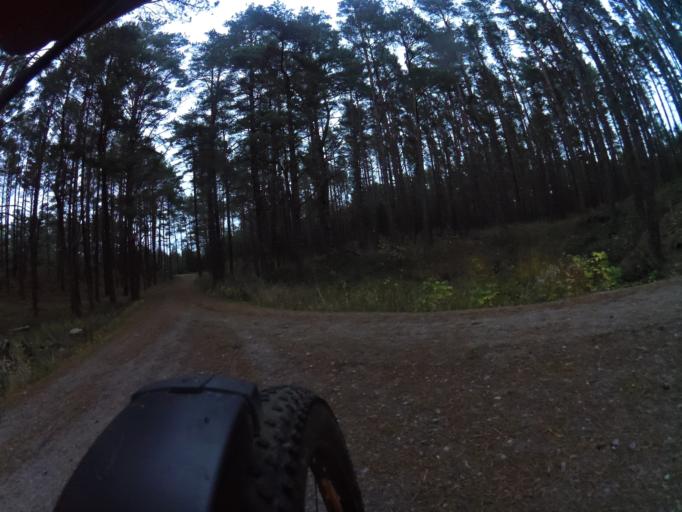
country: PL
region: Pomeranian Voivodeship
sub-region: Powiat wejherowski
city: Choczewo
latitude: 54.8029
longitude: 17.7890
